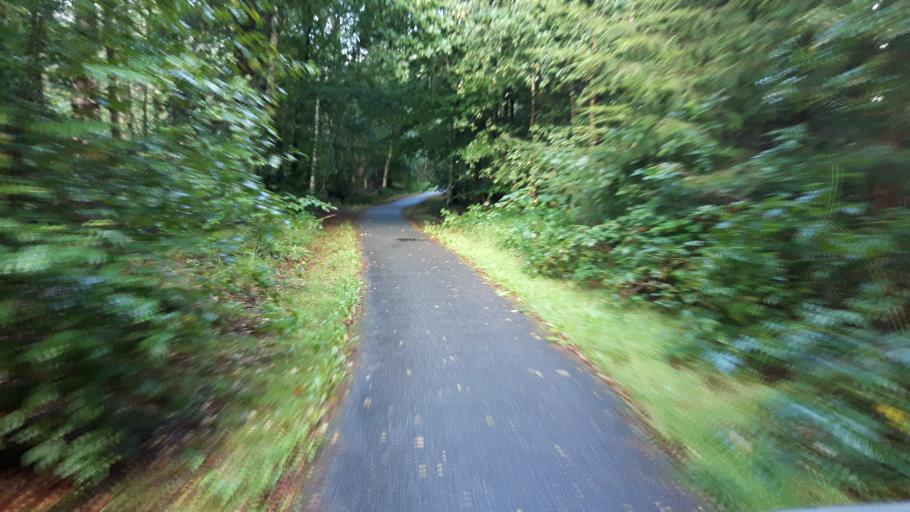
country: NL
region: Friesland
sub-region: Gemeente Smallingerland
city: Drachten
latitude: 53.0667
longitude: 6.1134
